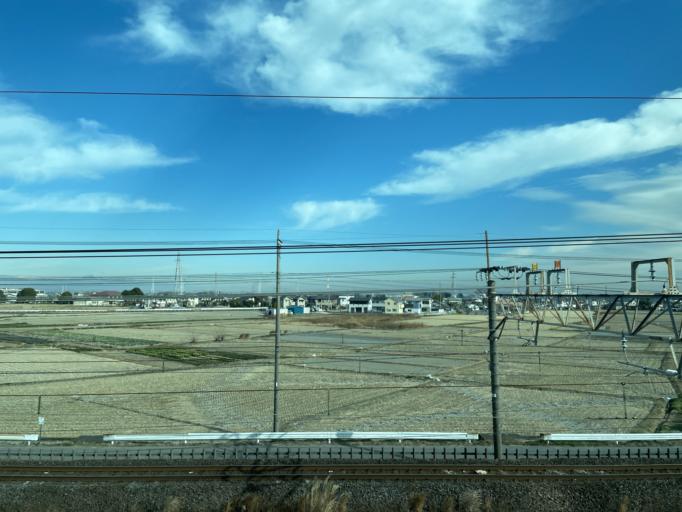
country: JP
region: Saitama
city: Kumagaya
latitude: 36.1631
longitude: 139.3521
